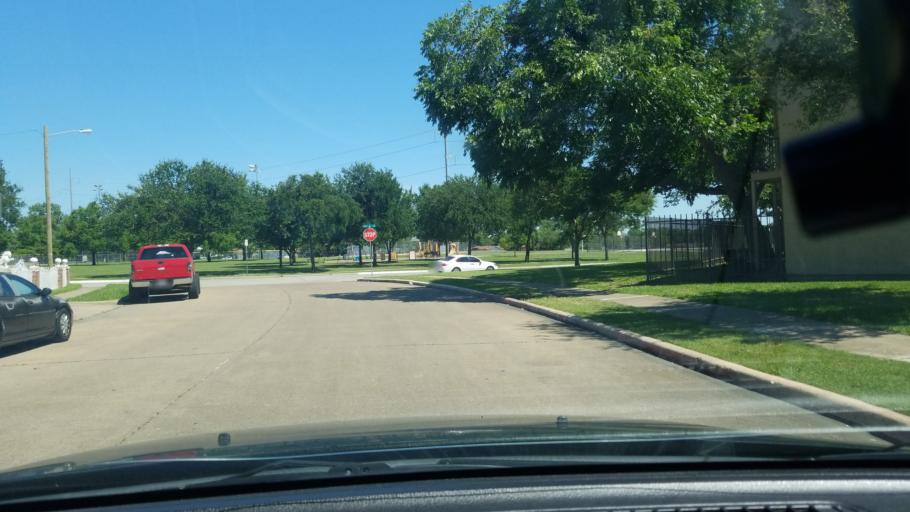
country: US
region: Texas
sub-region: Dallas County
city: Mesquite
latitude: 32.7769
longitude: -96.6116
